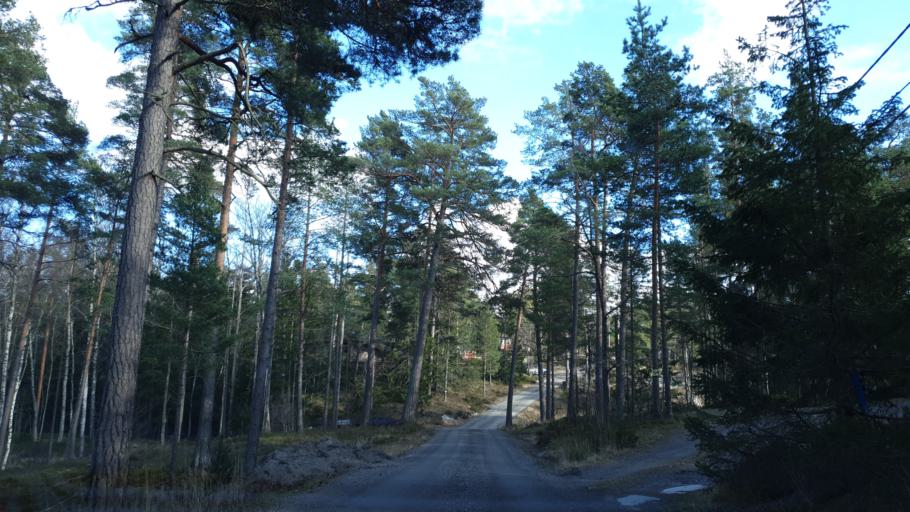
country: SE
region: Stockholm
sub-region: Varmdo Kommun
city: Holo
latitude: 59.2718
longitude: 18.6383
